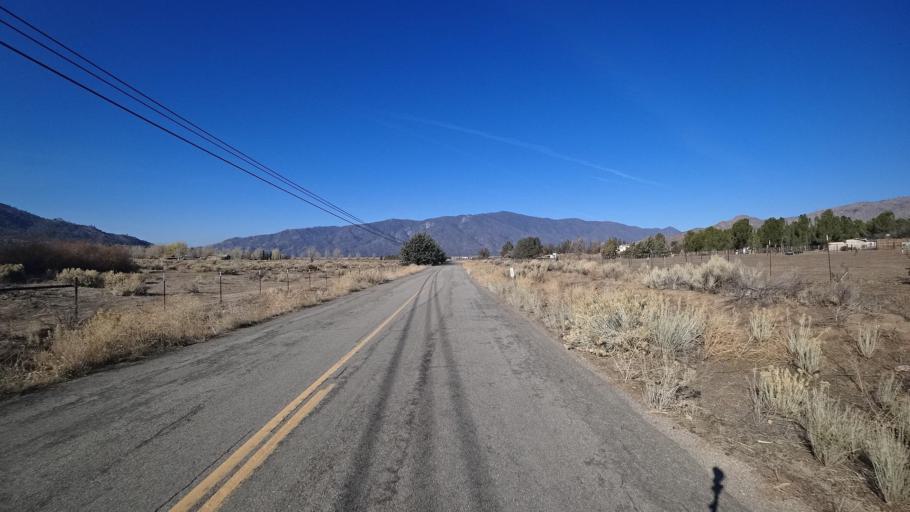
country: US
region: California
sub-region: Kern County
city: Bodfish
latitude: 35.4045
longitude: -118.4864
